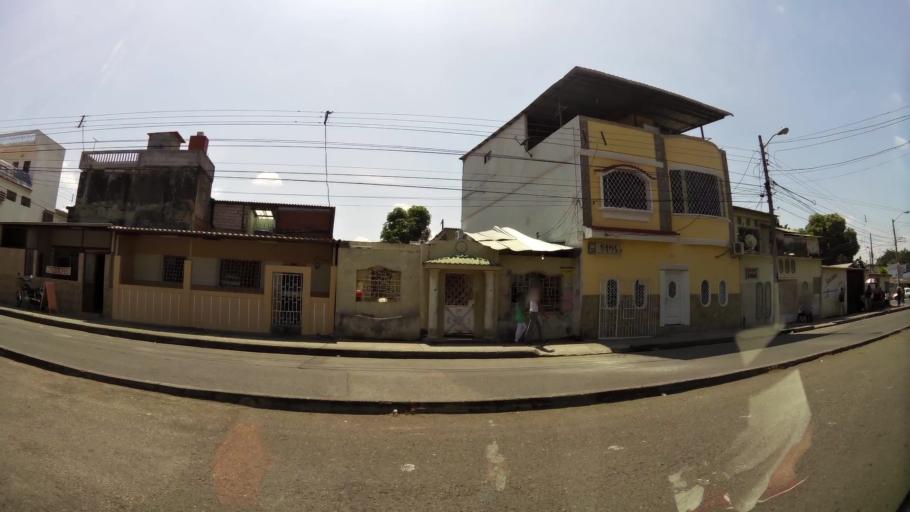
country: EC
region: Guayas
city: Guayaquil
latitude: -2.2351
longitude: -79.9043
